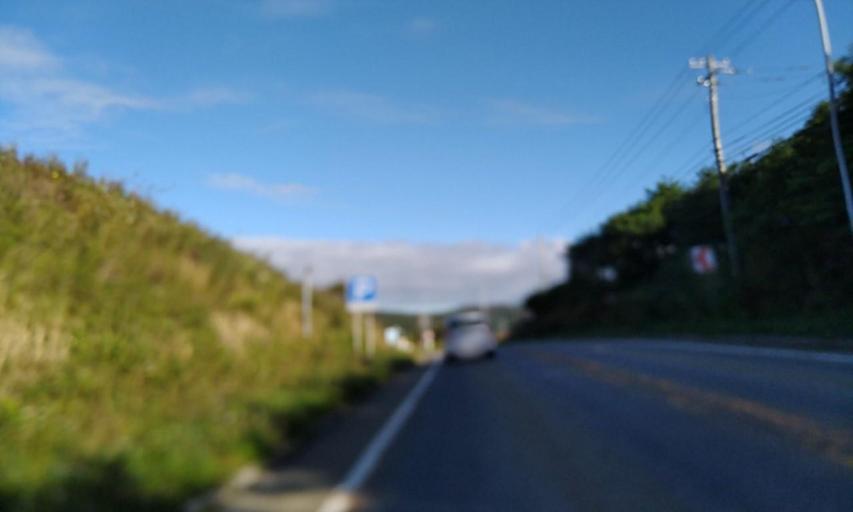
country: JP
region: Hokkaido
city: Shizunai-furukawacho
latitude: 42.1824
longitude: 142.7276
